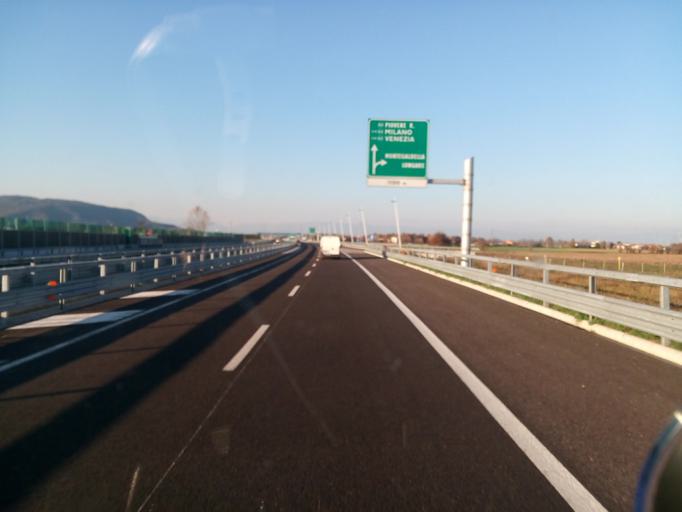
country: IT
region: Veneto
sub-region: Provincia di Vicenza
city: Villaganzerla
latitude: 45.4361
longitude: 11.6358
